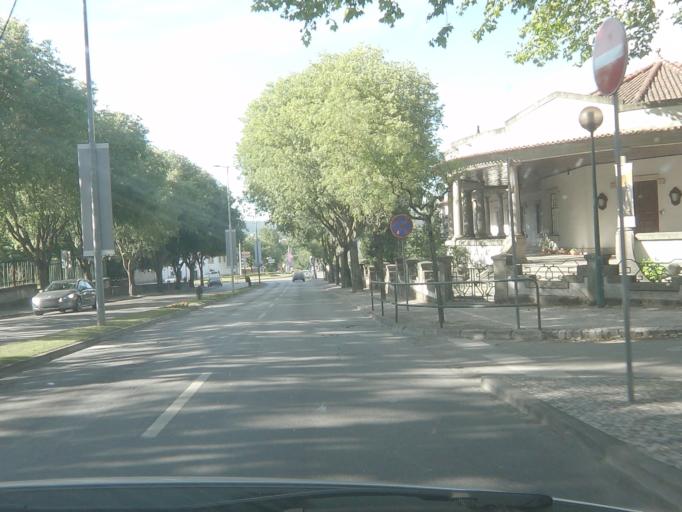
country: PT
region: Viseu
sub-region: Viseu
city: Viseu
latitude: 40.6586
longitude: -7.9058
